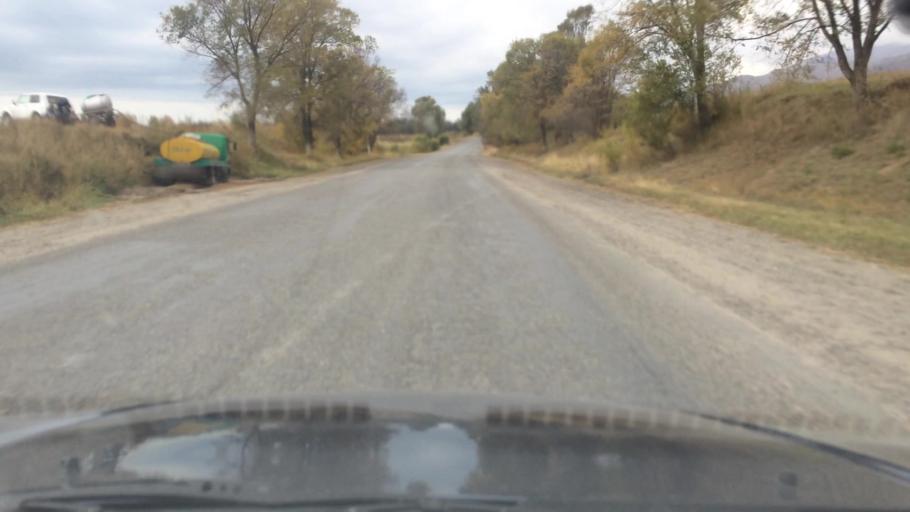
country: KG
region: Ysyk-Koel
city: Tyup
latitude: 42.7828
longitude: 78.2323
